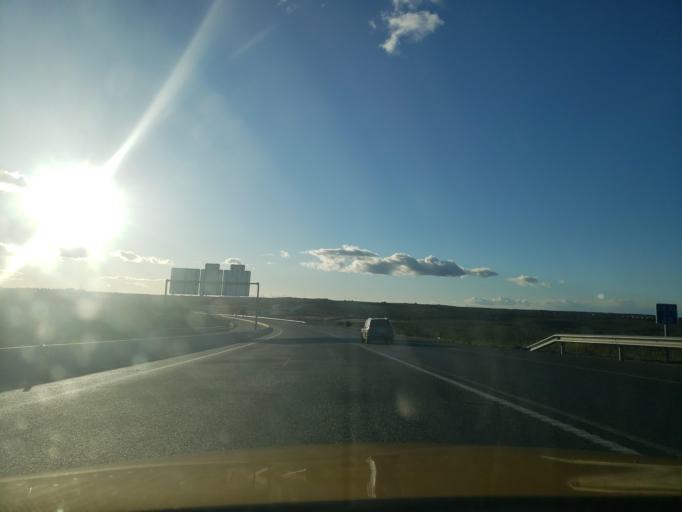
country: ES
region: Castille-La Mancha
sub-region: Province of Toledo
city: Burguillos de Toledo
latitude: 39.8157
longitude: -3.9894
